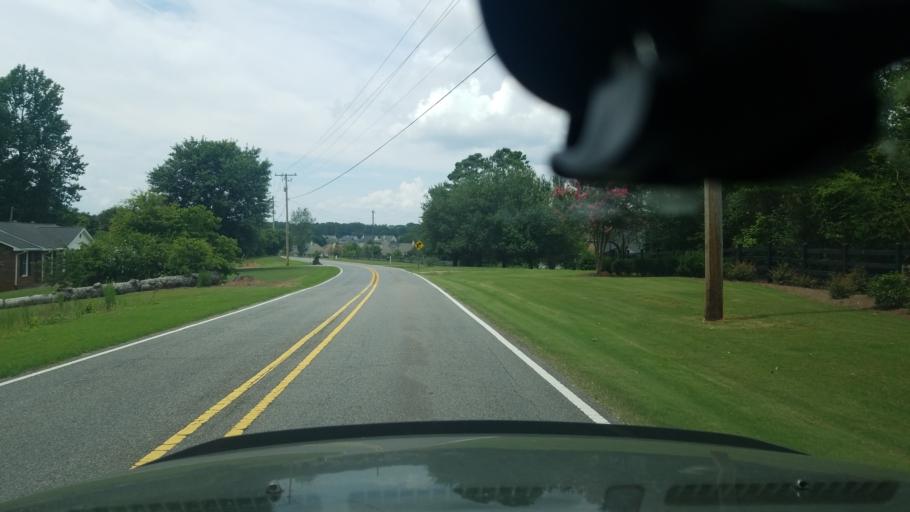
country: US
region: Georgia
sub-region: Forsyth County
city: Cumming
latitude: 34.2283
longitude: -84.2134
